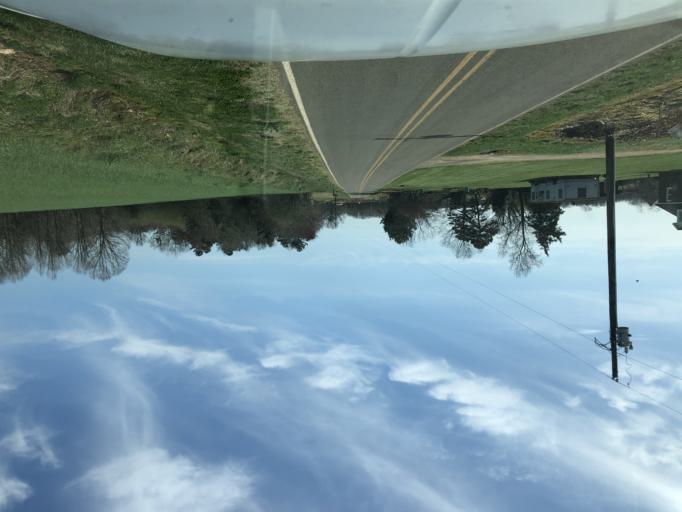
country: US
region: North Carolina
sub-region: Cleveland County
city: Shelby
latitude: 35.4837
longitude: -81.6409
